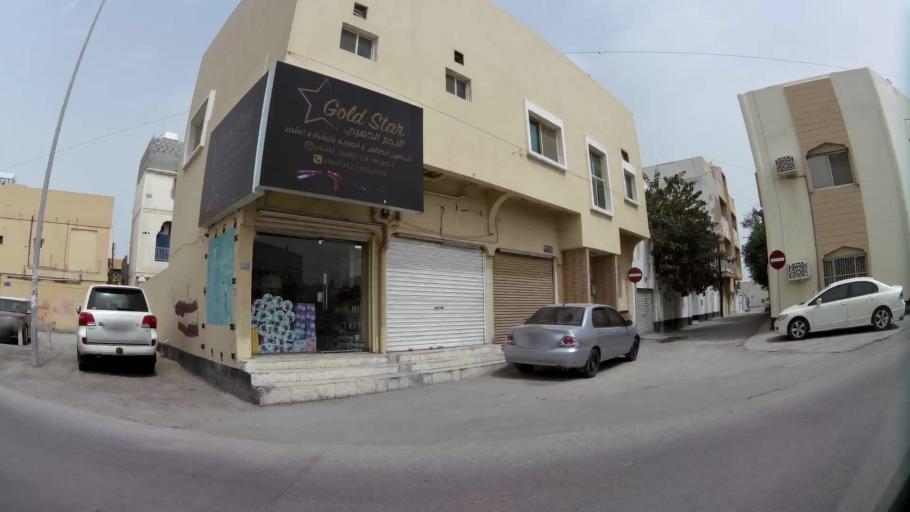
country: BH
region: Northern
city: Madinat `Isa
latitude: 26.1795
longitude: 50.5505
